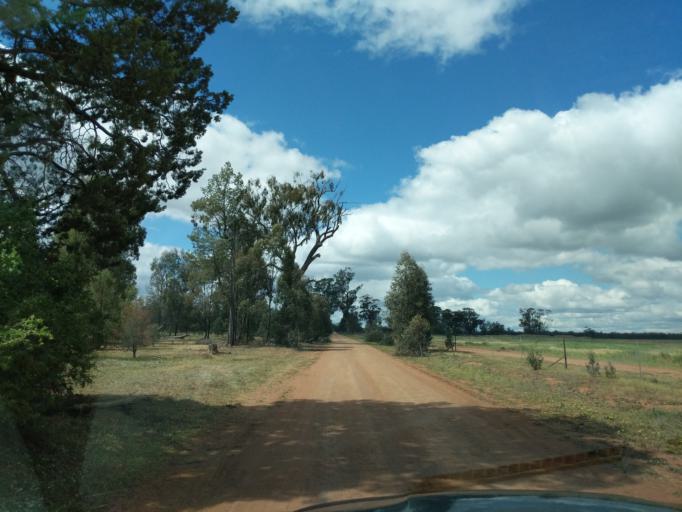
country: AU
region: New South Wales
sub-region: Coolamon
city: Coolamon
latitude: -34.8542
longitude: 146.9015
